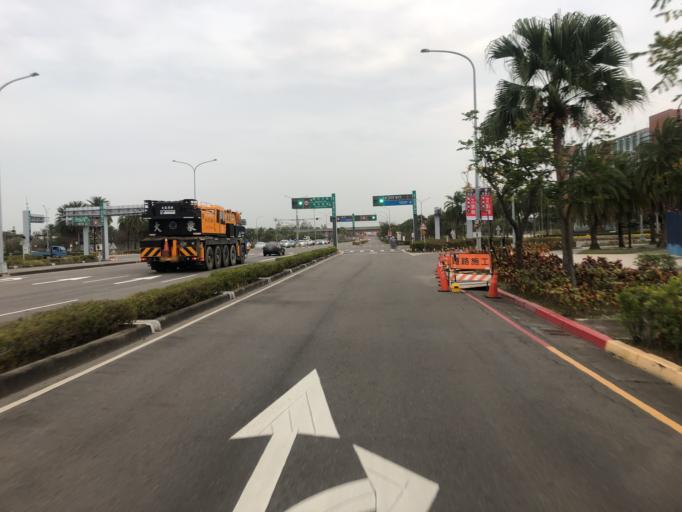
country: TW
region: Taiwan
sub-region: Tainan
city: Tainan
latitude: 23.1019
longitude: 120.2793
